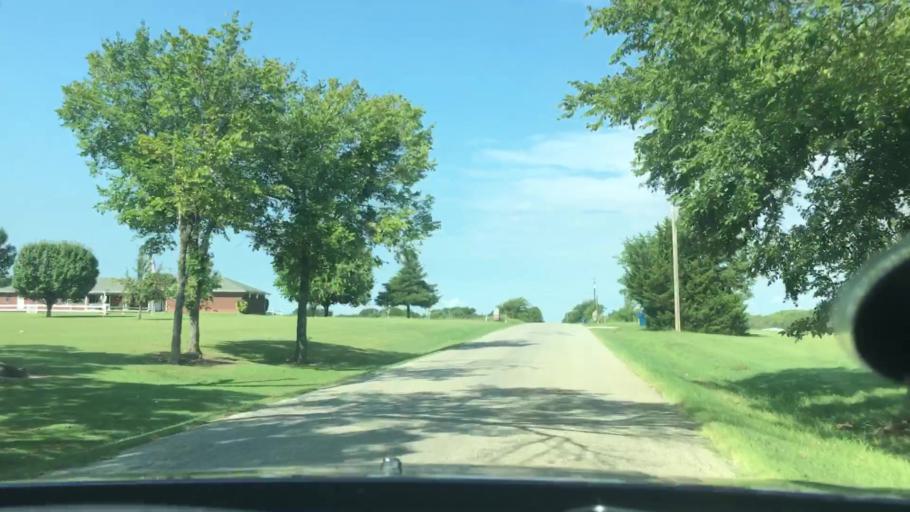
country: US
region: Oklahoma
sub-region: Bryan County
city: Calera
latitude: 33.9110
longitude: -96.4814
